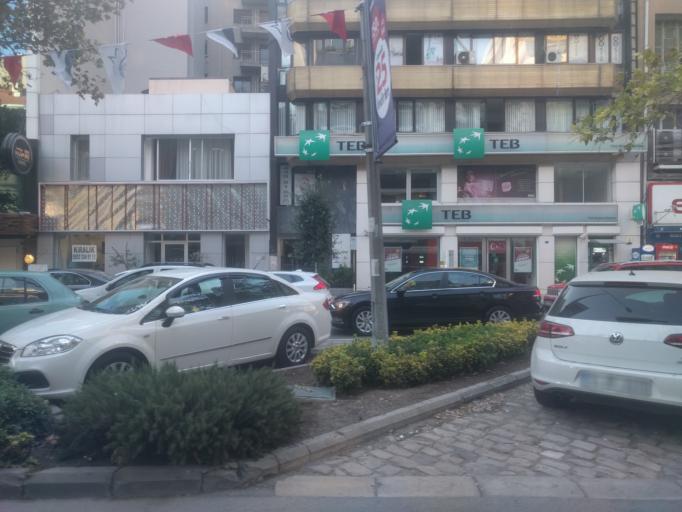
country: TR
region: Izmir
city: Izmir
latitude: 38.4279
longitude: 27.1334
